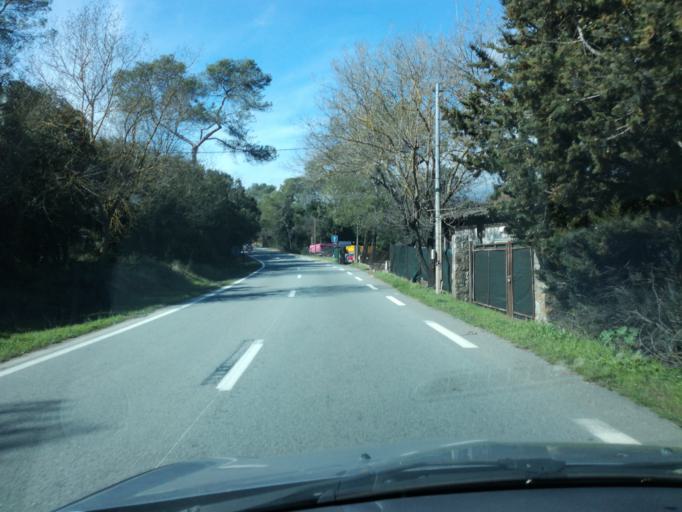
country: FR
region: Provence-Alpes-Cote d'Azur
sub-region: Departement des Alpes-Maritimes
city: Vallauris
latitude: 43.6087
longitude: 7.0547
